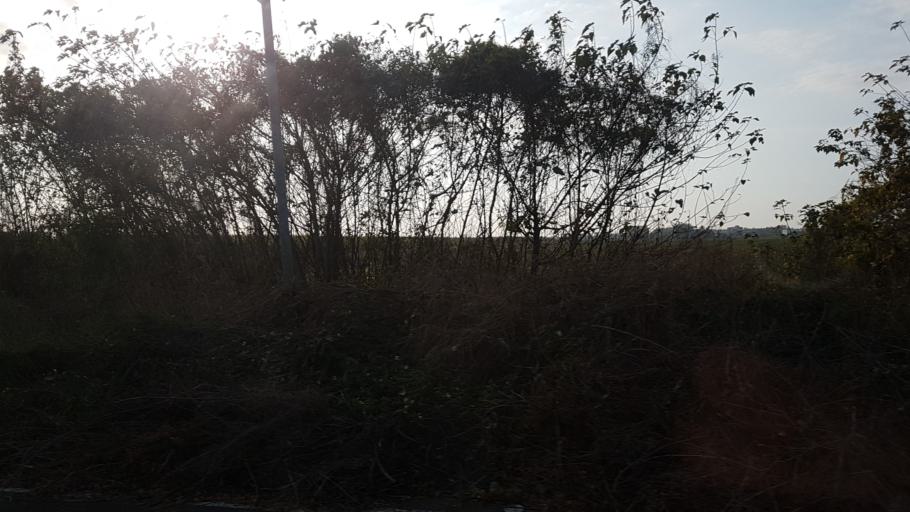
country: TW
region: Taiwan
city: Xinying
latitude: 23.3467
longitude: 120.3739
